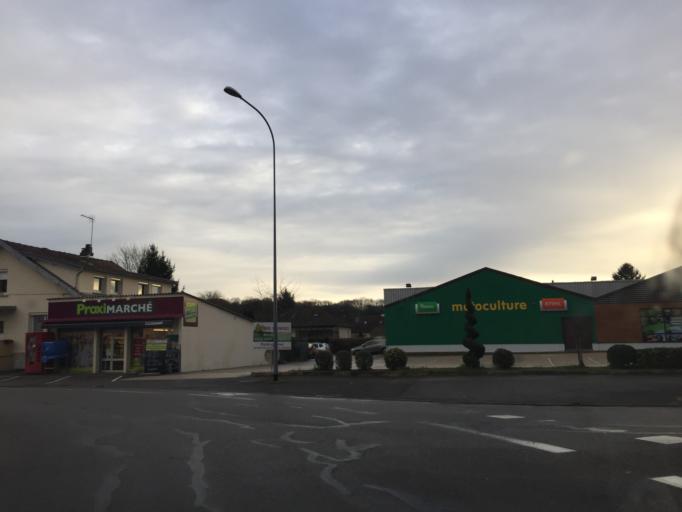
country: FR
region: Franche-Comte
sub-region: Departement du Jura
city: Dole
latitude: 47.0728
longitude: 5.4975
